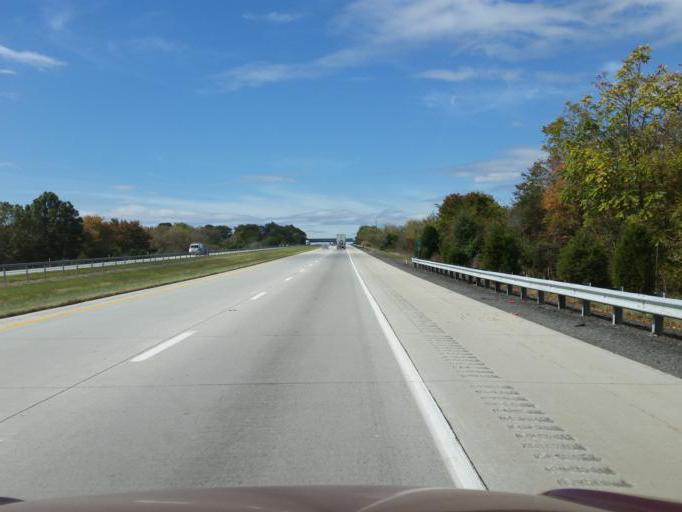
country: US
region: Pennsylvania
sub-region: Dauphin County
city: Middletown
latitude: 40.1945
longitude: -76.6673
